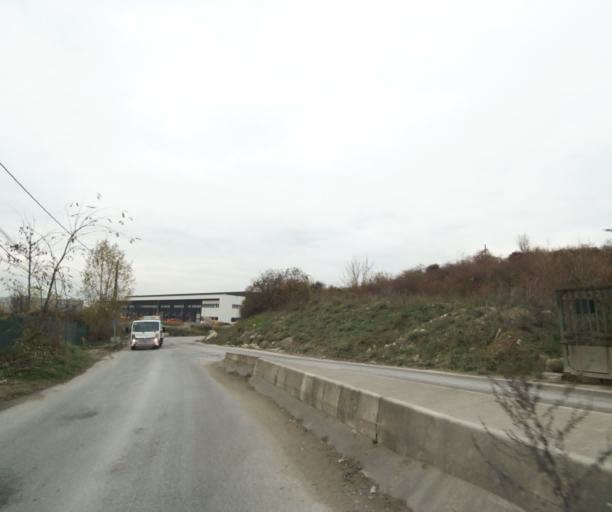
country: FR
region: Ile-de-France
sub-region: Departement de Seine-Saint-Denis
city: Le Blanc-Mesnil
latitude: 48.9653
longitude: 2.4654
